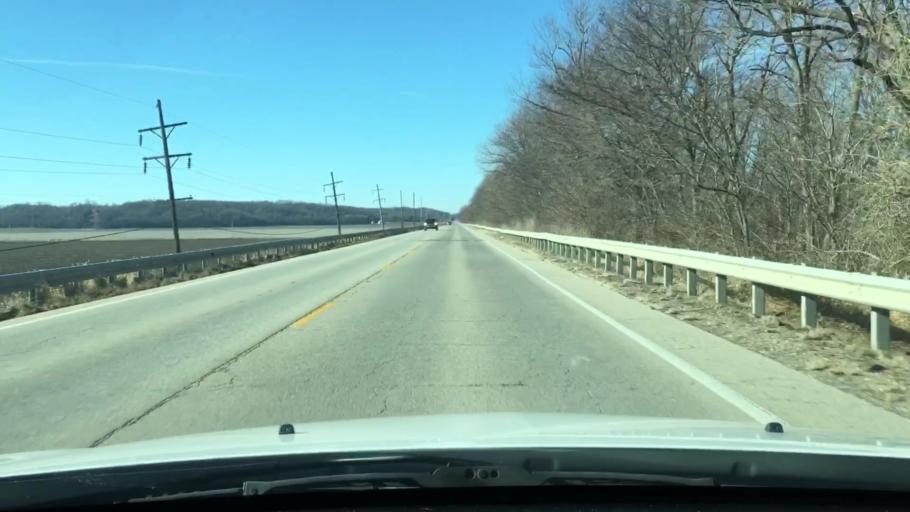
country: US
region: Illinois
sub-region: Mason County
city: Havana
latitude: 40.3006
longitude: -90.1098
